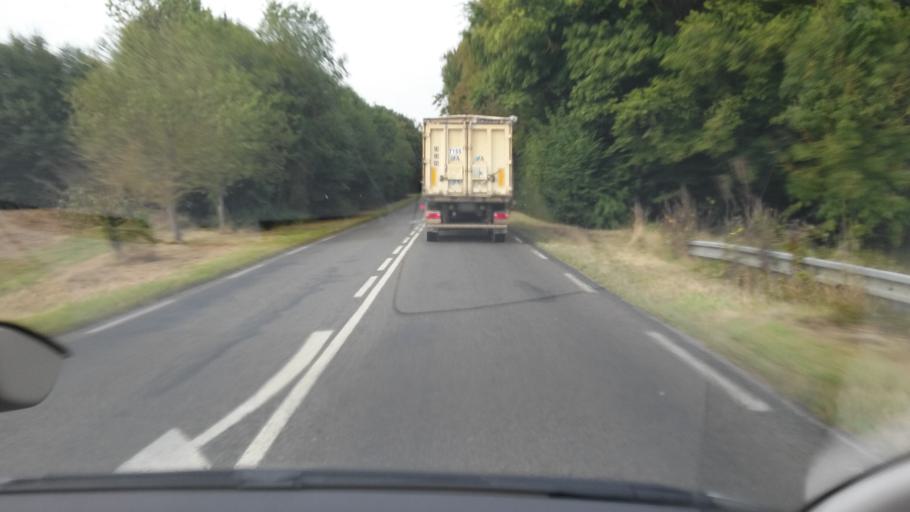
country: FR
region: Champagne-Ardenne
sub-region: Departement de la Marne
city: Verzenay
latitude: 49.1089
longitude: 4.1125
